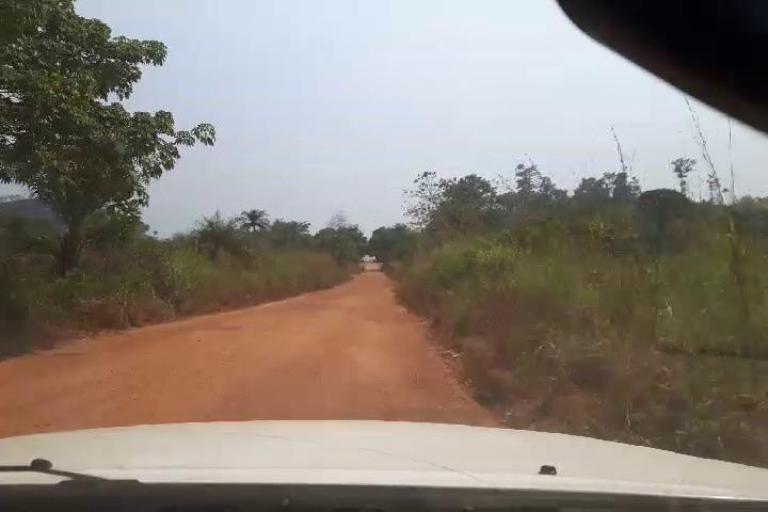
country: SL
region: Northern Province
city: Bumbuna
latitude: 9.0167
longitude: -11.7655
